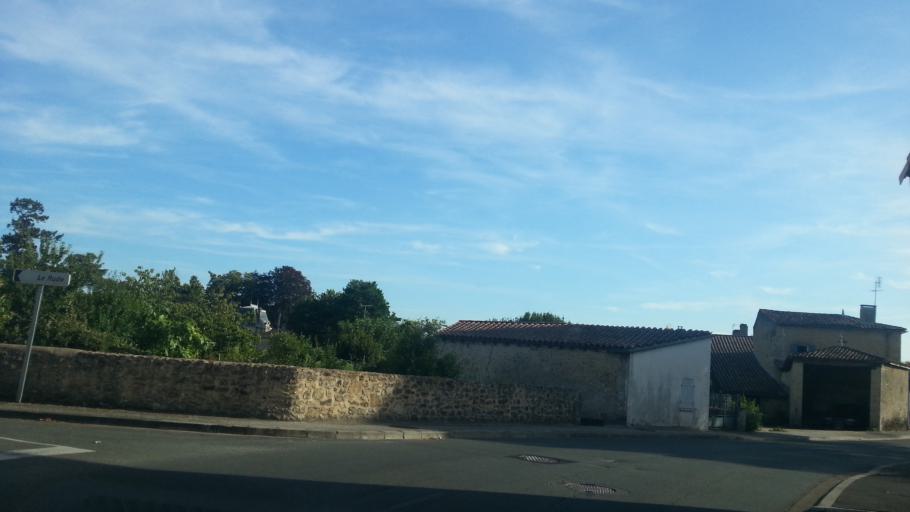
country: FR
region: Aquitaine
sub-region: Departement de la Gironde
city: Illats
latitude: 44.5995
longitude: -0.3701
